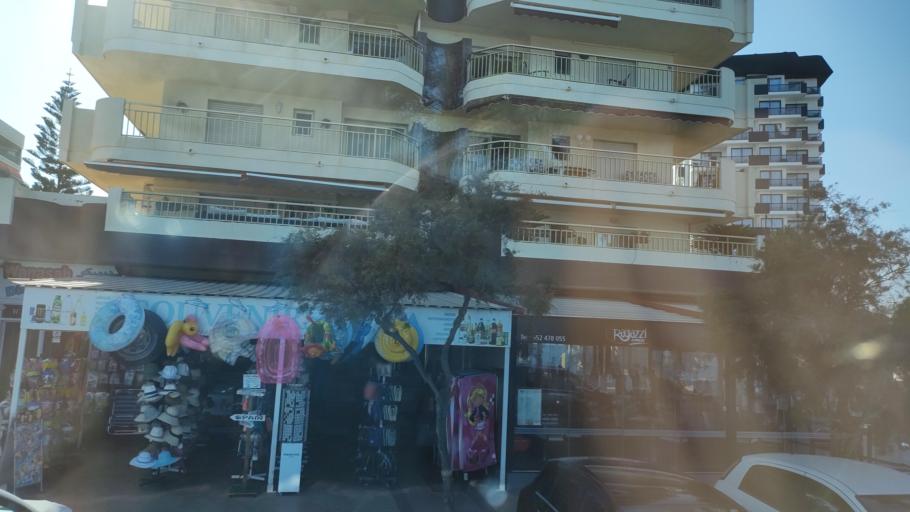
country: ES
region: Andalusia
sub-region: Provincia de Malaga
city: Fuengirola
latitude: 36.5310
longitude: -4.6247
